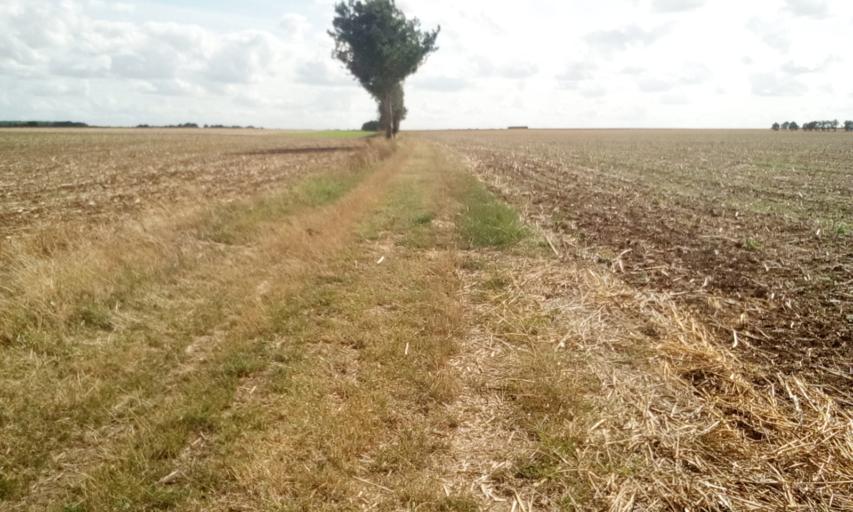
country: FR
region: Lower Normandy
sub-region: Departement du Calvados
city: Saint-Sylvain
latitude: 49.0870
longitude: -0.1967
